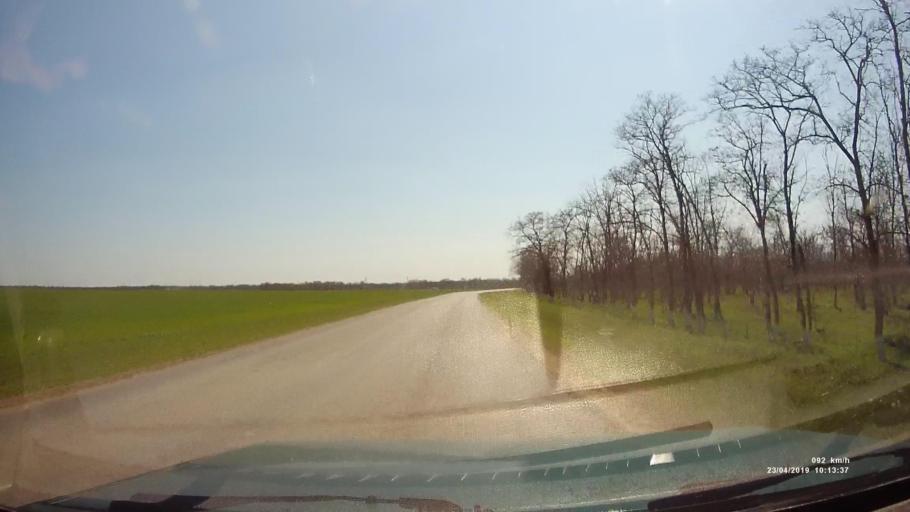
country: RU
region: Rostov
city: Sovetskoye
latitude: 46.6839
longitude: 42.3587
